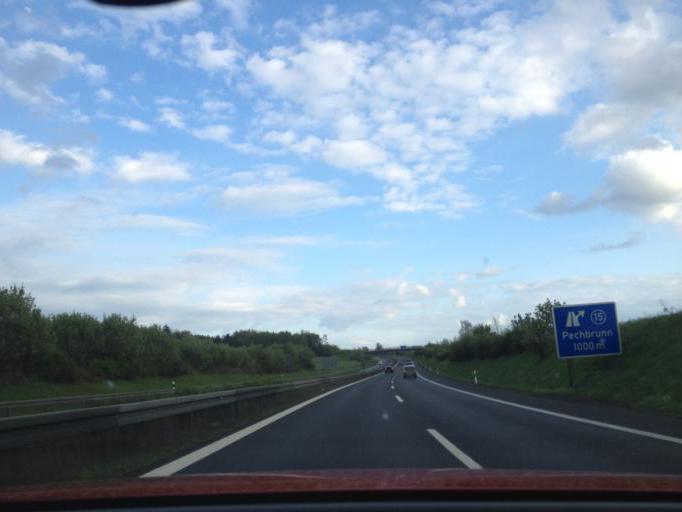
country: DE
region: Bavaria
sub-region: Upper Palatinate
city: Pechbrunn
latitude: 49.9889
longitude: 12.1283
